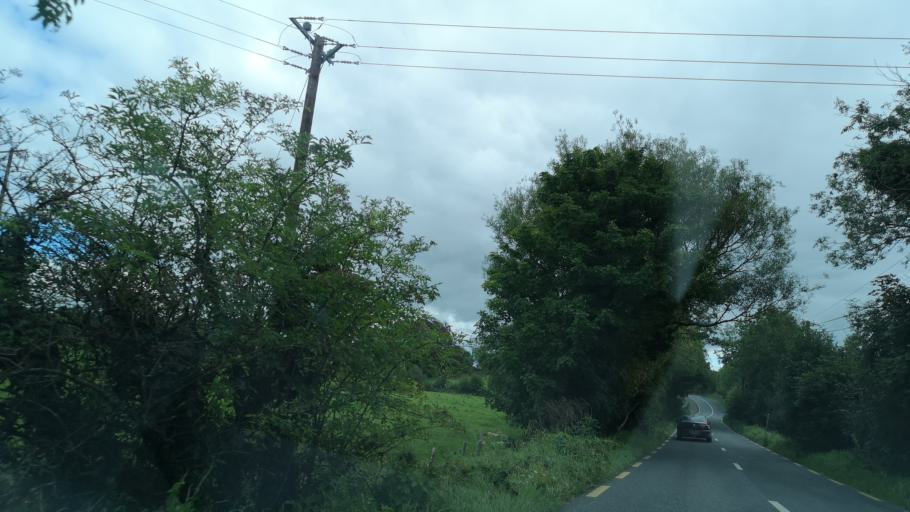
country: IE
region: Leinster
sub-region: Uibh Fhaili
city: Banagher
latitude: 53.2797
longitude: -8.0635
